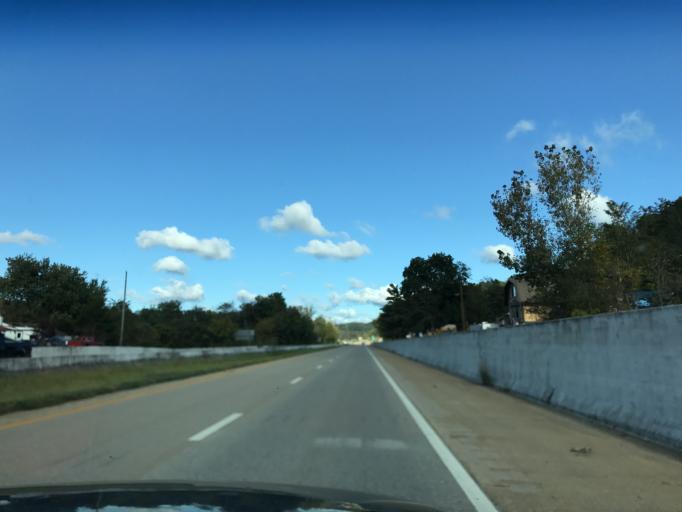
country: US
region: Ohio
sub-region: Athens County
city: Athens
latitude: 39.3162
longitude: -81.9851
